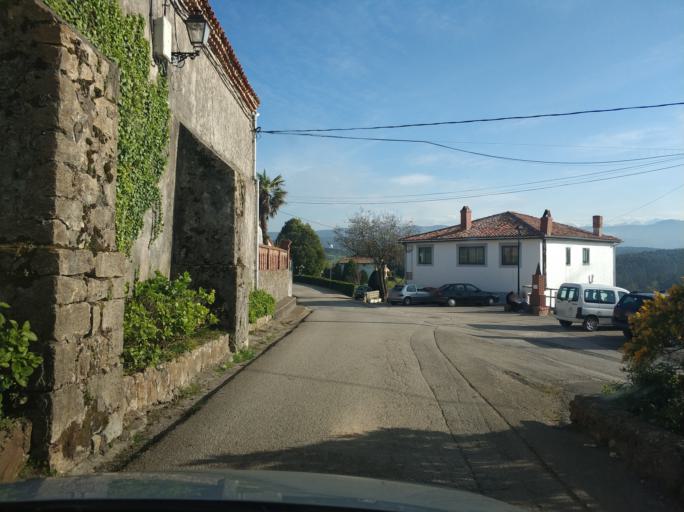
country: ES
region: Cantabria
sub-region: Provincia de Cantabria
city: Comillas
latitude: 43.3830
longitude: -4.3134
